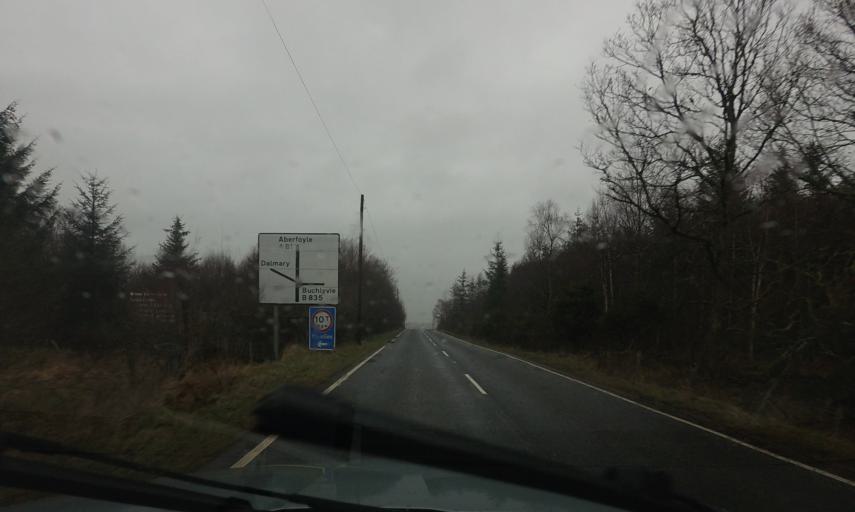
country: GB
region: Scotland
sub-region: Stirling
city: Balfron
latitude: 56.1188
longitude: -4.3592
